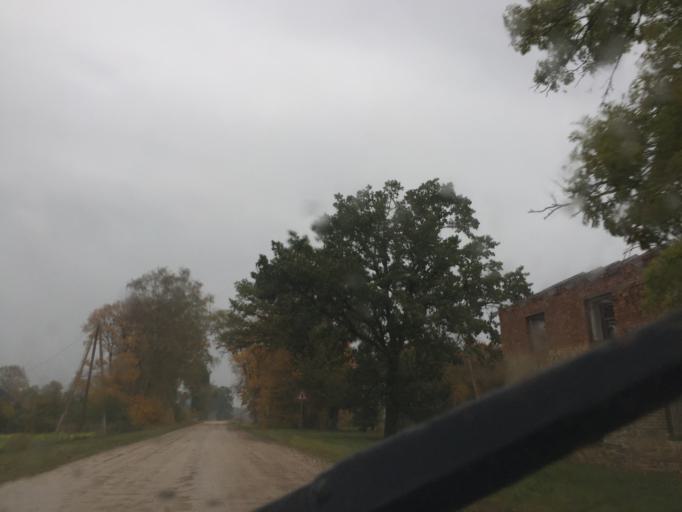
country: LV
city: Tireli
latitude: 56.7049
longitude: 23.4982
